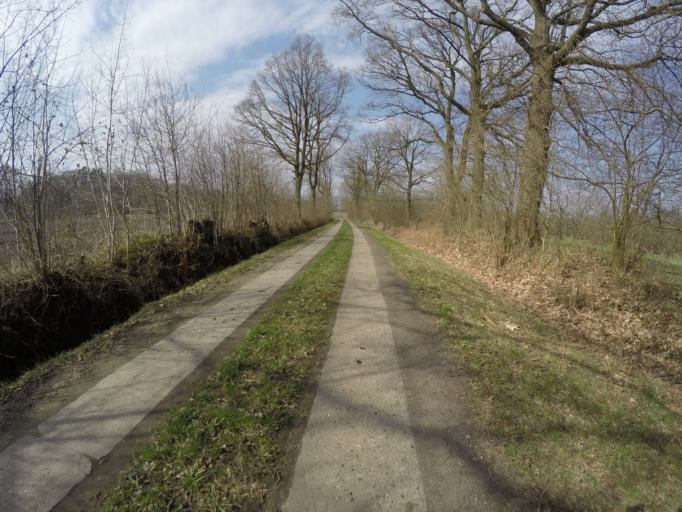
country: DE
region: Schleswig-Holstein
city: Borstel-Hohenraden
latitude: 53.7201
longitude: 9.8349
